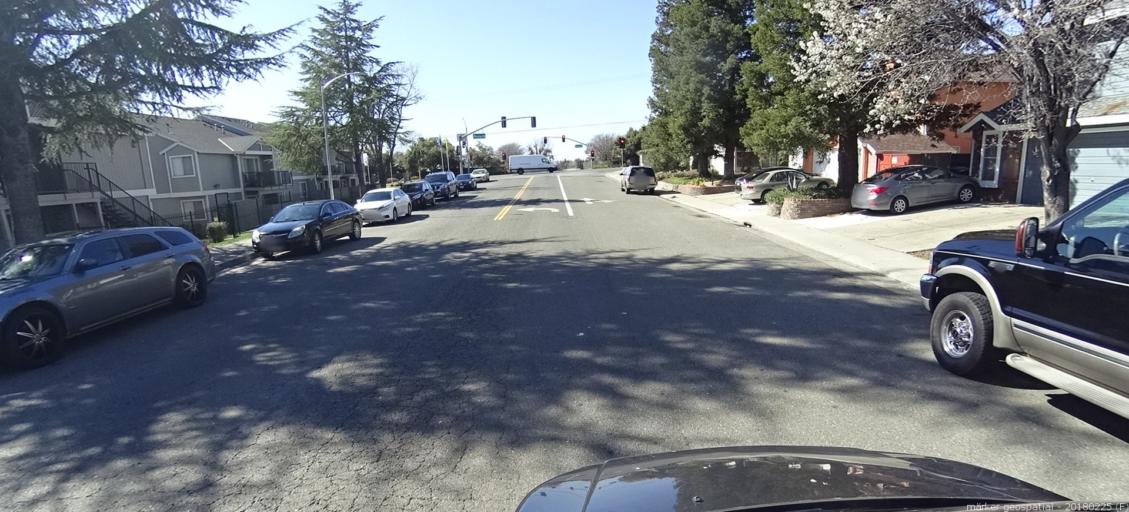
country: US
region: California
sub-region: Sacramento County
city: North Highlands
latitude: 38.7167
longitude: -121.3634
